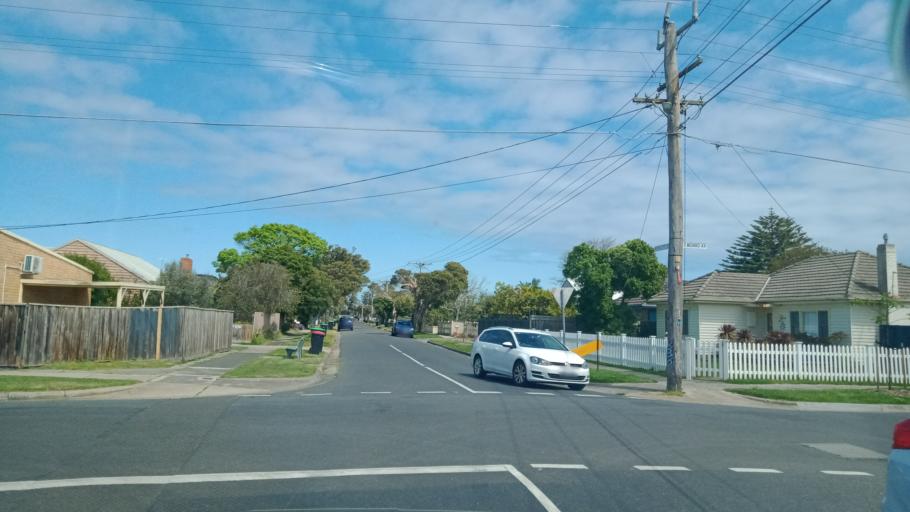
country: AU
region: Victoria
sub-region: Kingston
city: Edithvale
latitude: -38.0408
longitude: 145.1175
